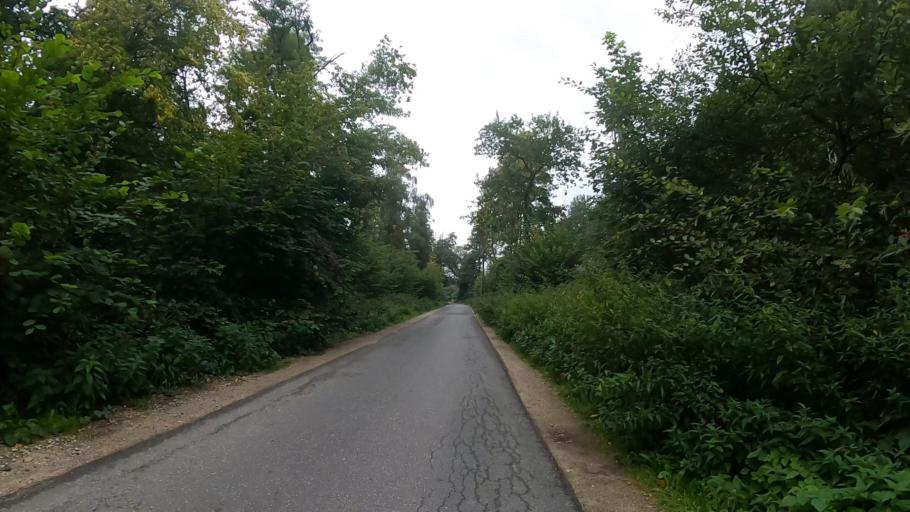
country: DE
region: Schleswig-Holstein
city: Prisdorf
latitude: 53.6723
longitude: 9.7666
